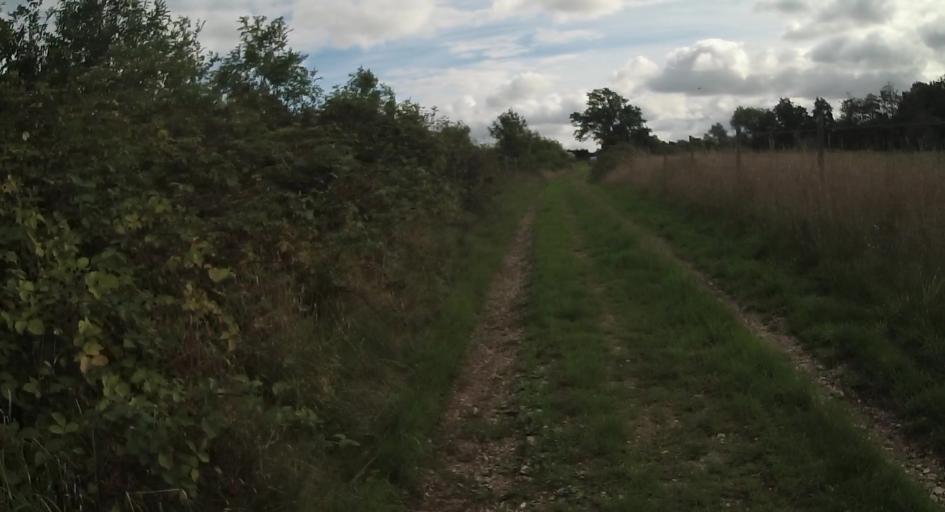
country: GB
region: England
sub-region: West Berkshire
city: Thatcham
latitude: 51.3838
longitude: -1.2399
